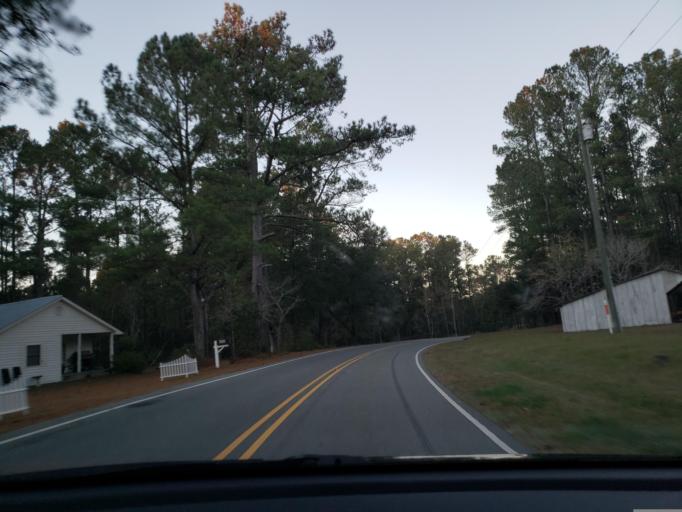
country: US
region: North Carolina
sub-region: Onslow County
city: Richlands
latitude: 34.7269
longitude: -77.6265
